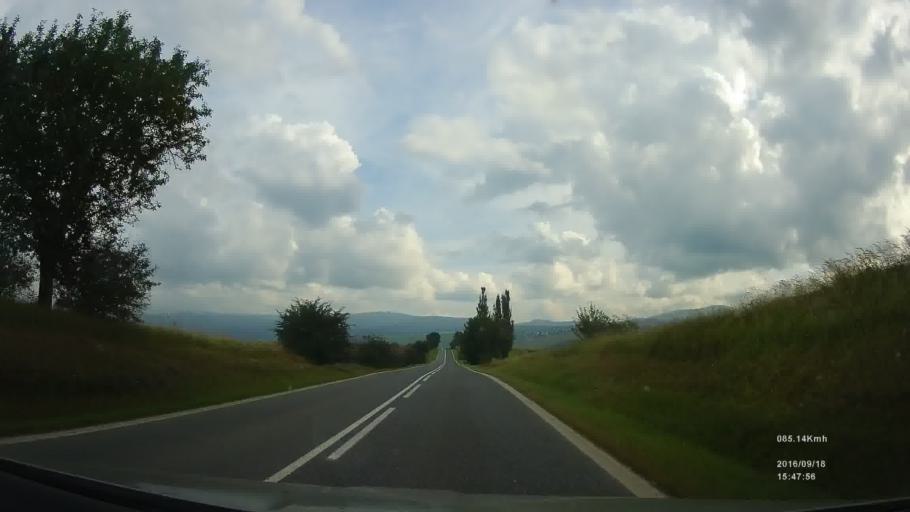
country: SK
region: Kosicky
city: Spisska Nova Ves
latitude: 48.9315
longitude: 20.5920
